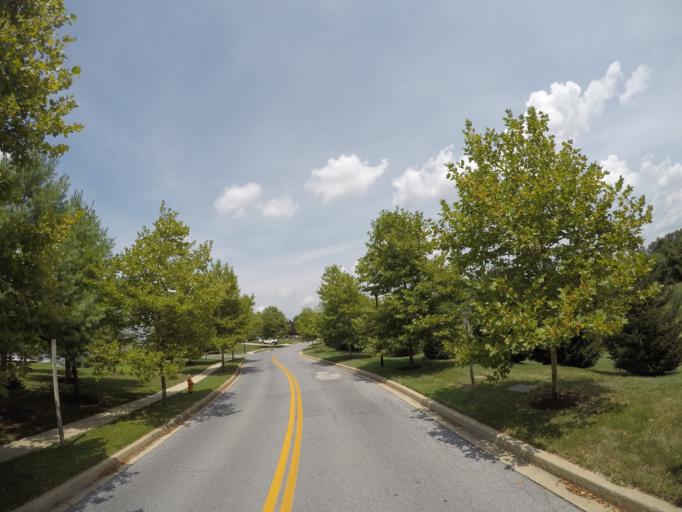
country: US
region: Maryland
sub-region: Howard County
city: North Laurel
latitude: 39.1428
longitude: -76.8566
